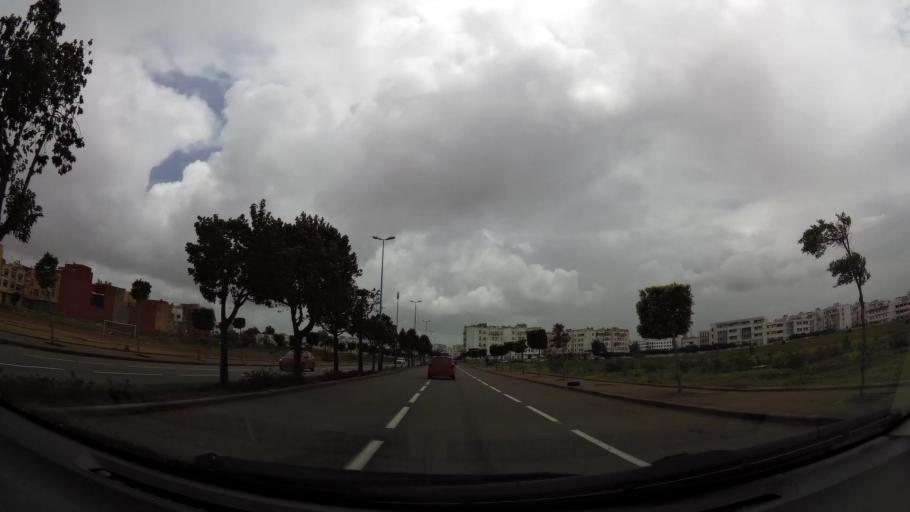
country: MA
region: Grand Casablanca
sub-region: Casablanca
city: Casablanca
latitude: 33.5473
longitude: -7.6870
